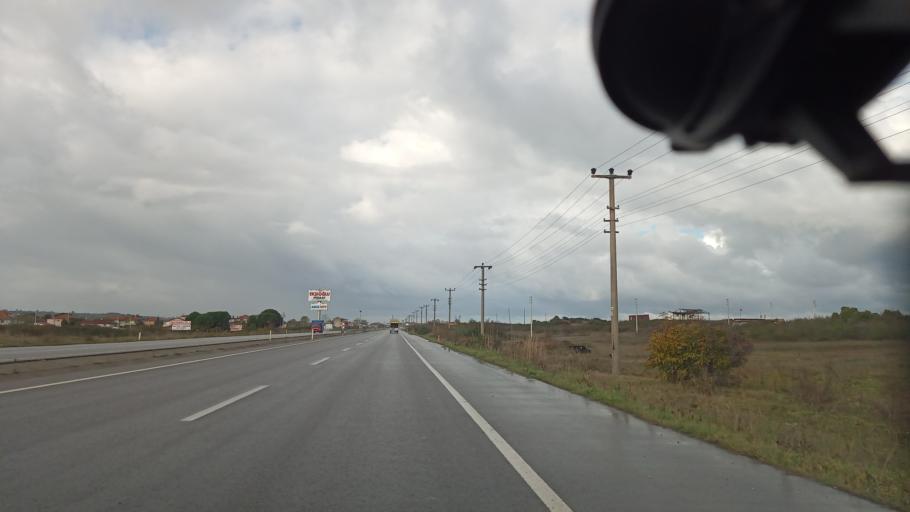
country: TR
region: Sakarya
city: Karasu
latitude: 41.0834
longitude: 30.7600
